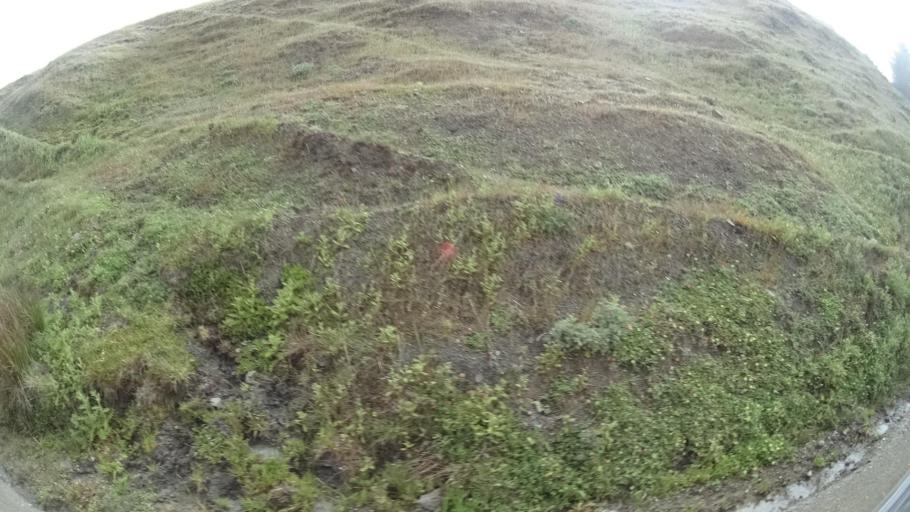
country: US
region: California
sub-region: Humboldt County
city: Redway
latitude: 40.2007
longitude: -123.7112
